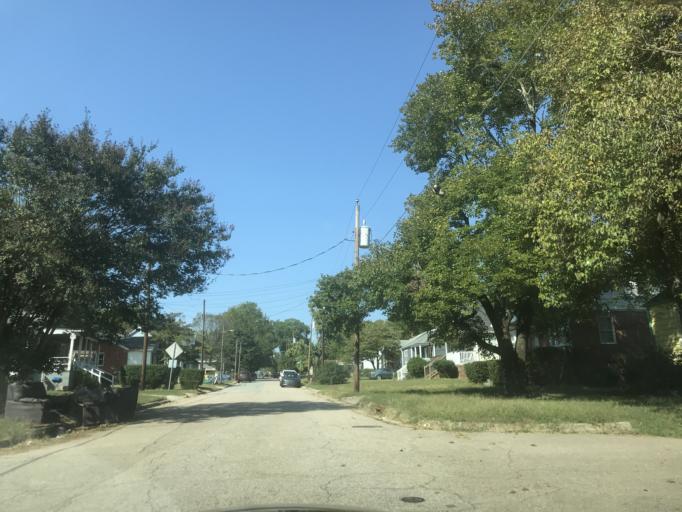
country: US
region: North Carolina
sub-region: Wake County
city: Raleigh
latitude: 35.7689
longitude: -78.6226
